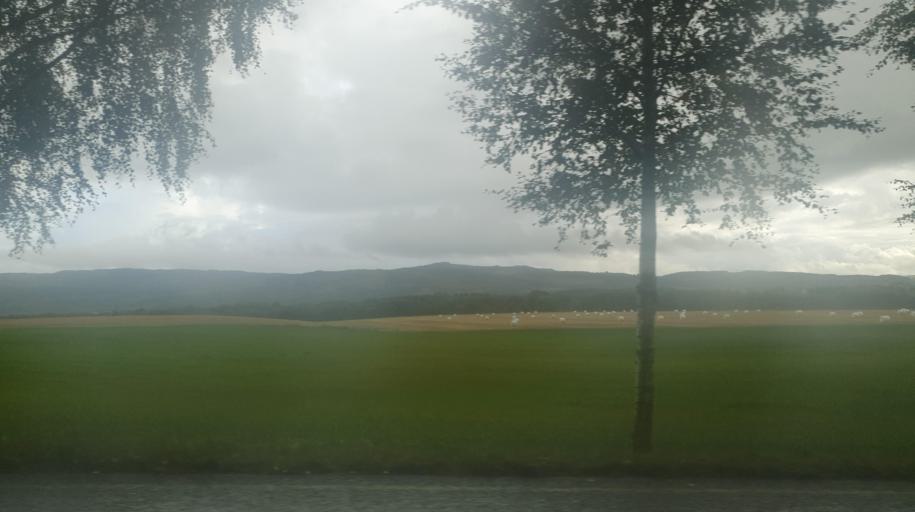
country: NO
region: Nord-Trondelag
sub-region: Verdal
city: Verdal
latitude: 63.7943
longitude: 11.5427
